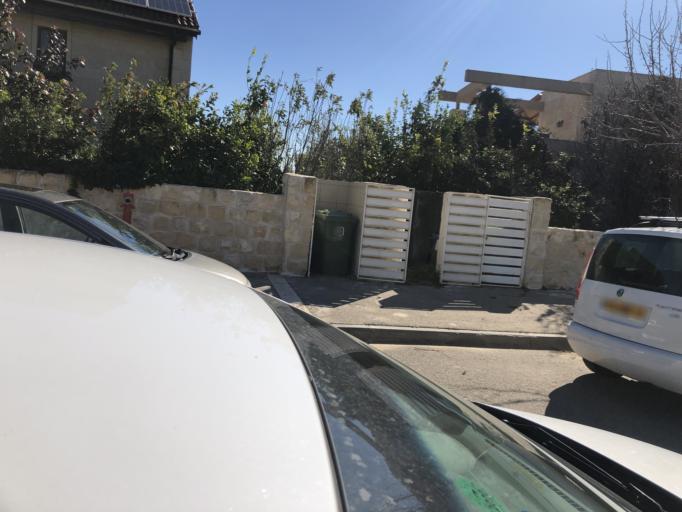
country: IL
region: Jerusalem
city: Zur Hadassa
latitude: 31.7431
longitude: 35.0534
